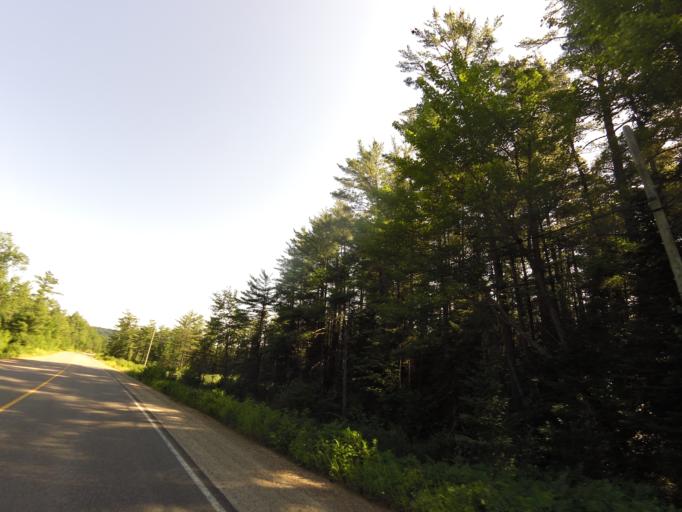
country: CA
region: Ontario
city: Deep River
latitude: 46.1846
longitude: -77.6806
